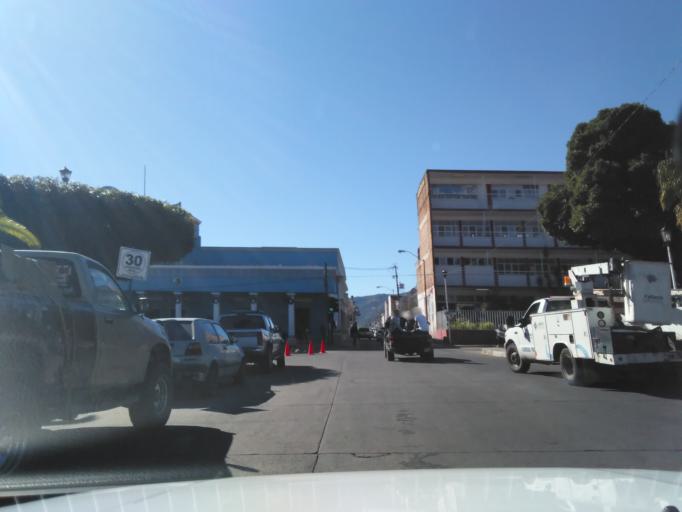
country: MX
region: Nayarit
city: Xalisco
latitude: 21.4443
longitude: -104.8998
